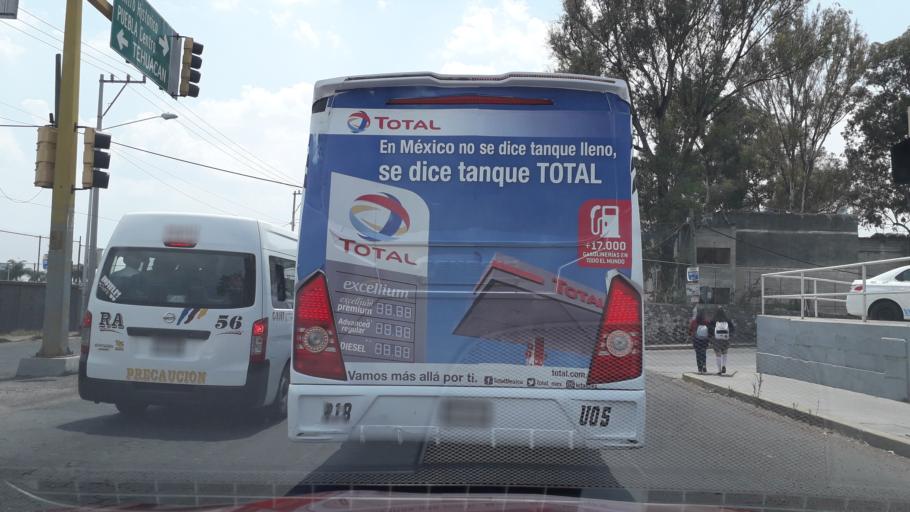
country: MX
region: Puebla
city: Puebla
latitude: 19.0488
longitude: -98.1702
